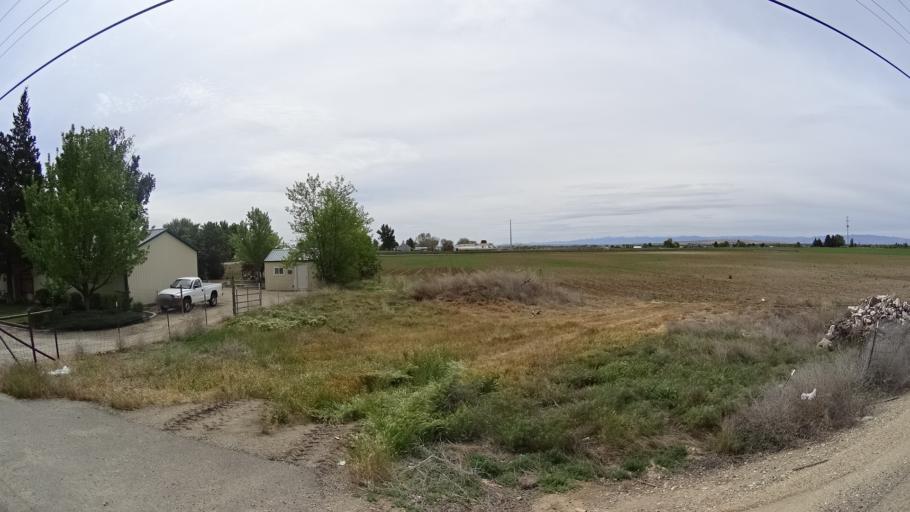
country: US
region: Idaho
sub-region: Ada County
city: Kuna
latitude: 43.5319
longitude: -116.3554
